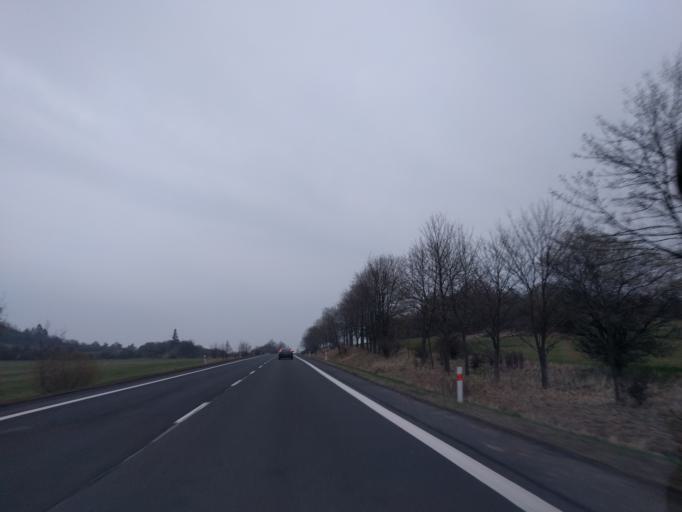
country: CZ
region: Karlovarsky
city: Zlutice
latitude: 50.1363
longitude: 13.1551
